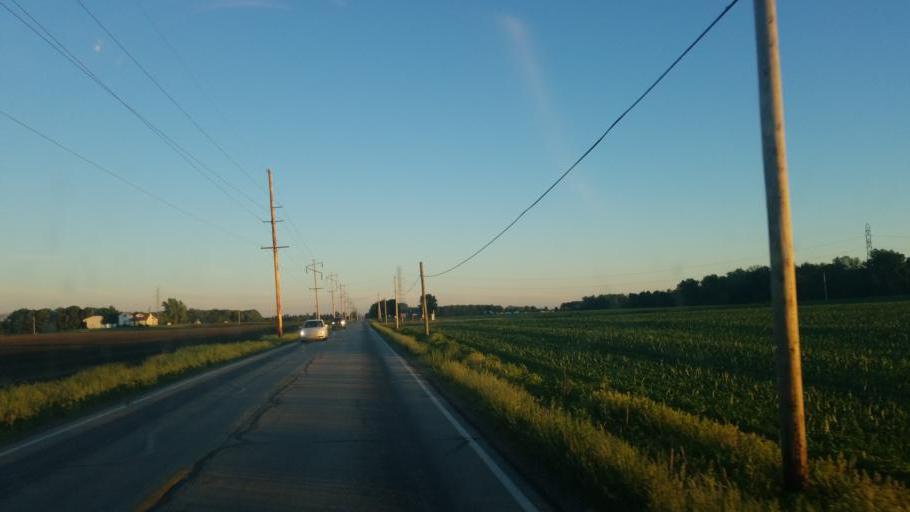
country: US
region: Indiana
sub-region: Elkhart County
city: Nappanee
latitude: 41.4067
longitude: -86.0011
